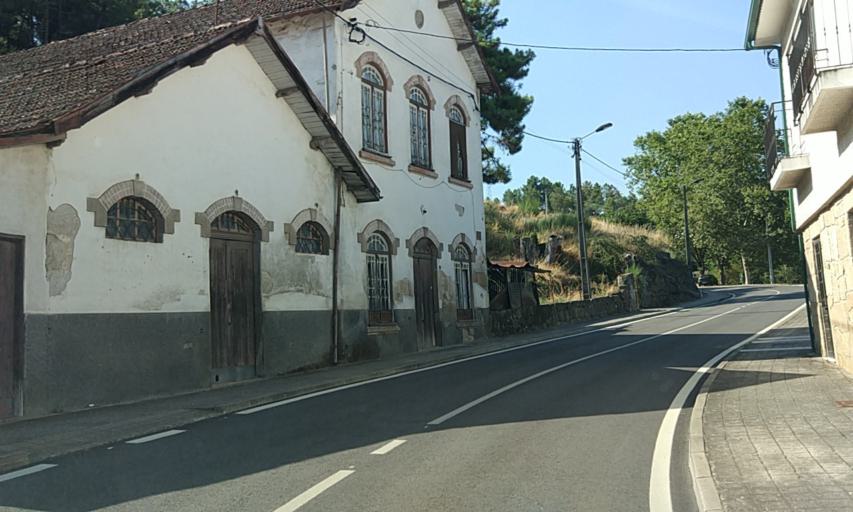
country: PT
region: Vila Real
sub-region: Sabrosa
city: Sabrosa
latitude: 41.2791
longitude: -7.4762
